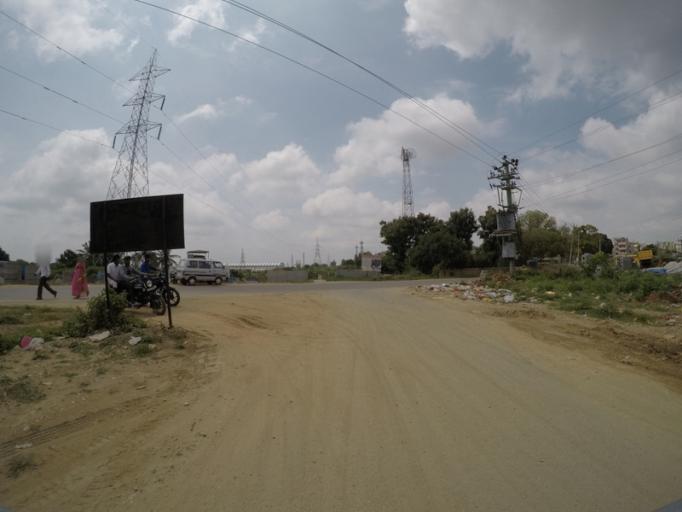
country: IN
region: Karnataka
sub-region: Bangalore Urban
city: Bangalore
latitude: 12.8489
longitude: 77.5168
